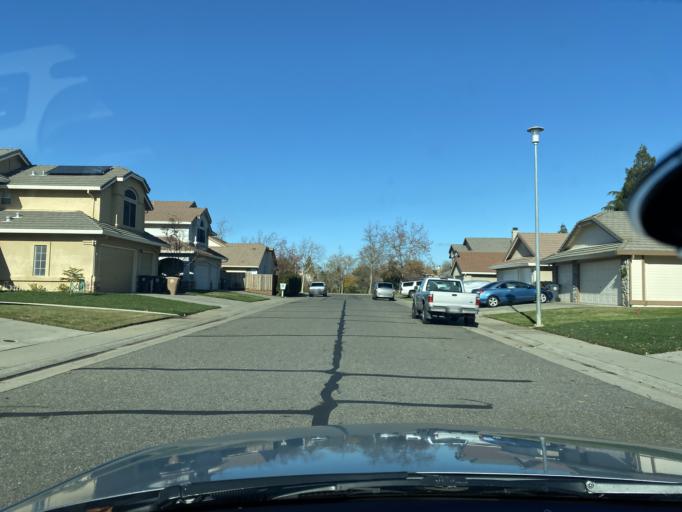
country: US
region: California
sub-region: Sacramento County
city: Elk Grove
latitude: 38.4332
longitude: -121.3815
